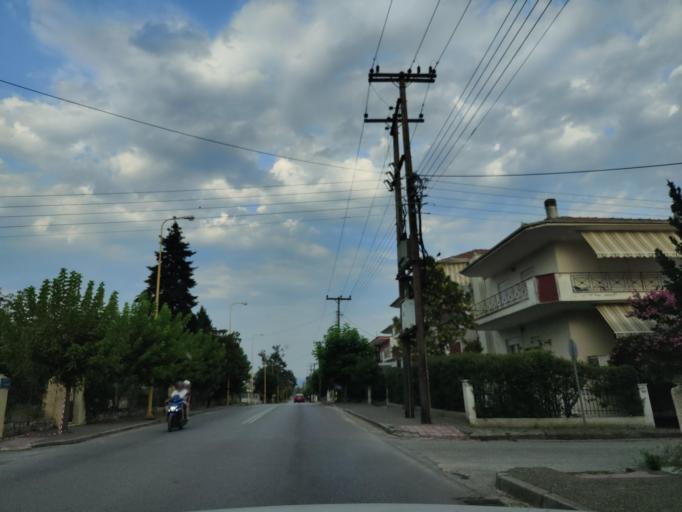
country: GR
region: East Macedonia and Thrace
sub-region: Nomos Dramas
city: Drama
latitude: 41.1537
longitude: 24.1168
